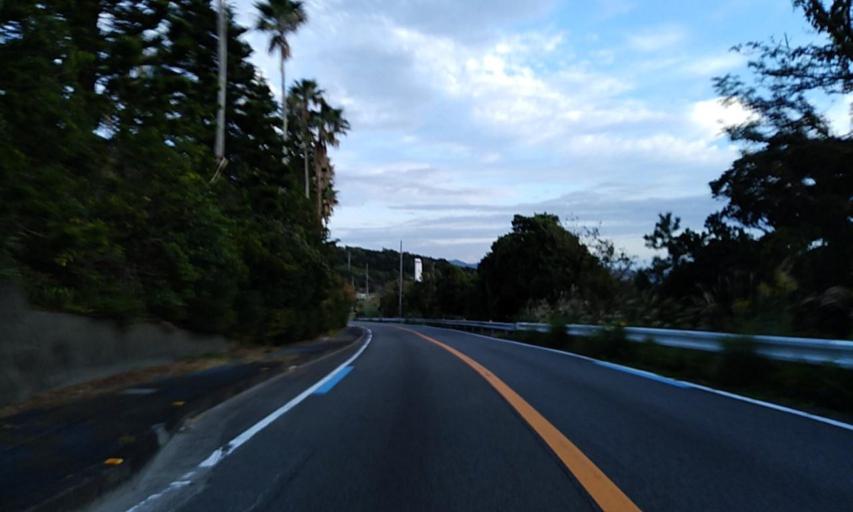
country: JP
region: Wakayama
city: Tanabe
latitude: 33.6657
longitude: 135.3378
